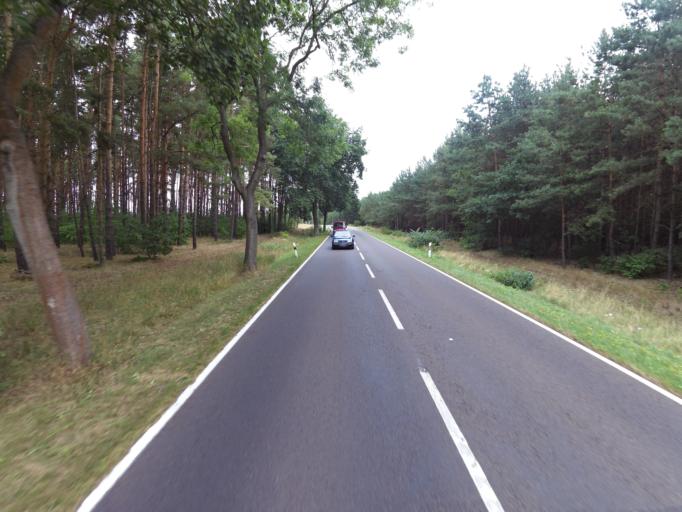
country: DE
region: Brandenburg
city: Liebenwalde
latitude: 52.9371
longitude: 13.3904
